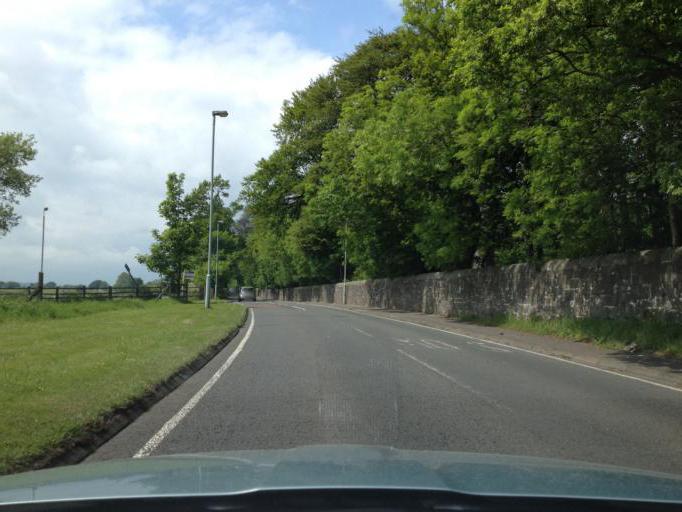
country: GB
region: Scotland
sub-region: West Dunbartonshire
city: Old Kilpatrick
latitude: 55.9136
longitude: -4.4754
